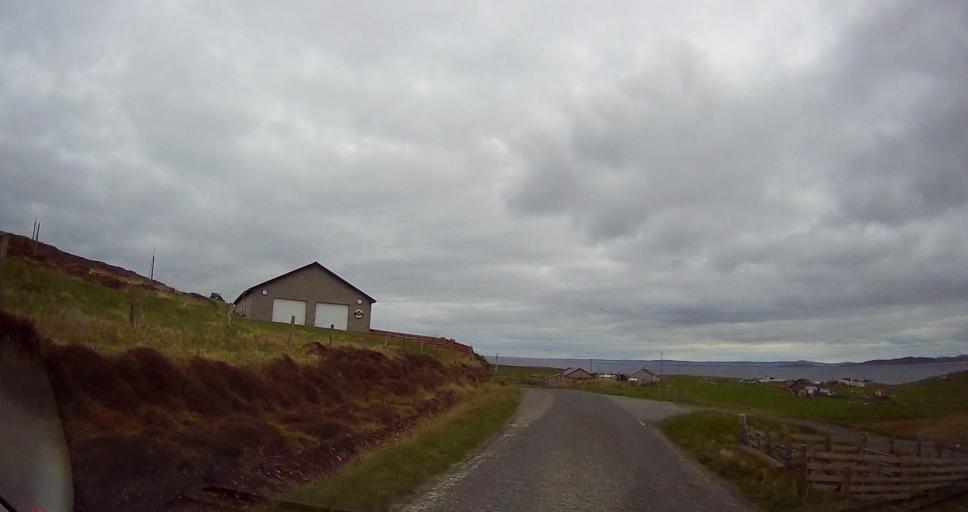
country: GB
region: Scotland
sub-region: Shetland Islands
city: Shetland
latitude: 60.5033
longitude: -1.0588
